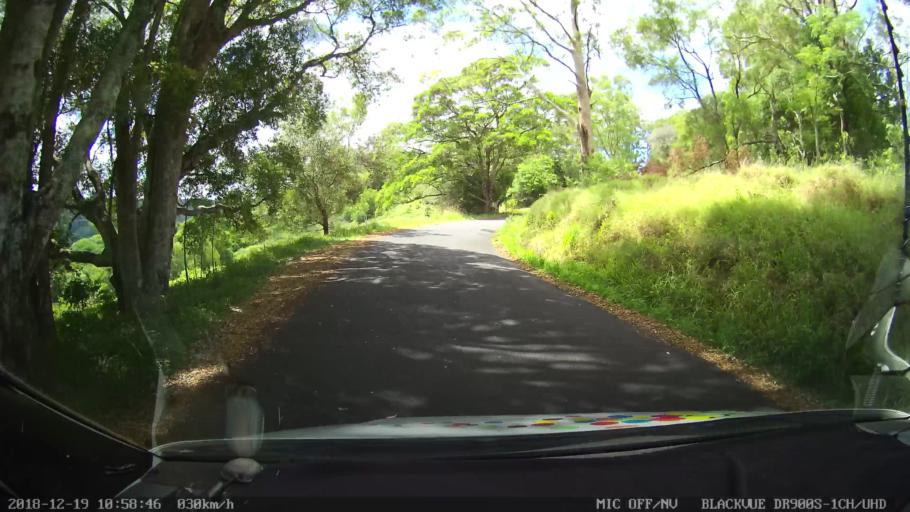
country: AU
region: New South Wales
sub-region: Lismore Municipality
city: Nimbin
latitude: -28.5939
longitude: 153.2633
